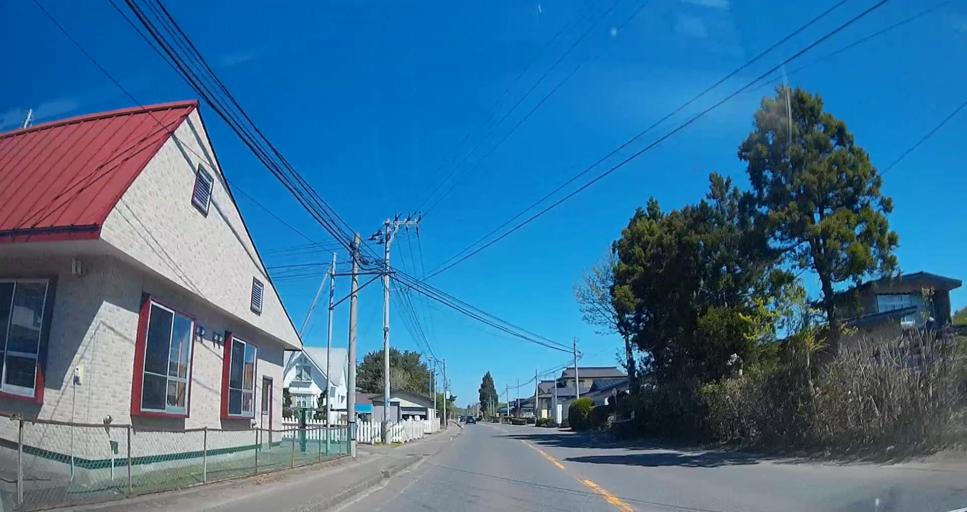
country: JP
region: Aomori
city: Misawa
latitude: 40.7918
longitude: 141.3999
